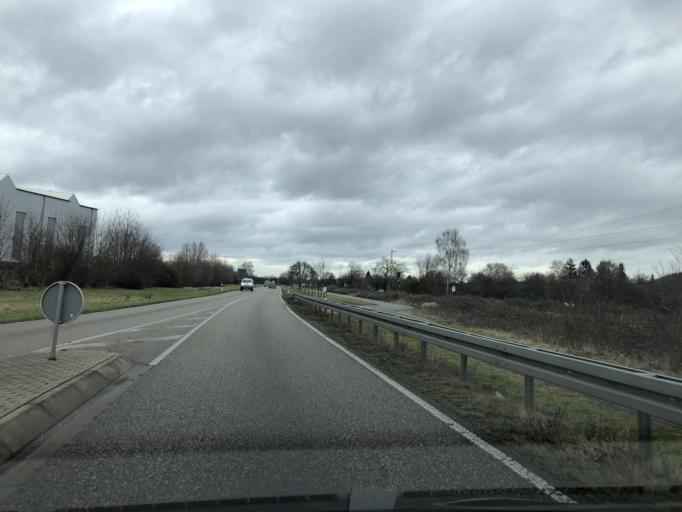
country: DE
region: Baden-Wuerttemberg
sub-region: Karlsruhe Region
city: Weingarten
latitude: 49.0135
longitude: 8.4778
